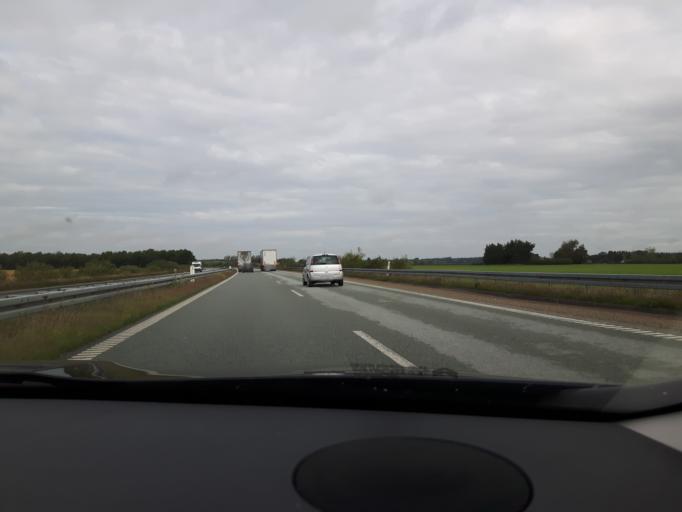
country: DK
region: North Denmark
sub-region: Hjorring Kommune
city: Hjorring
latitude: 57.4732
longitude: 10.0442
